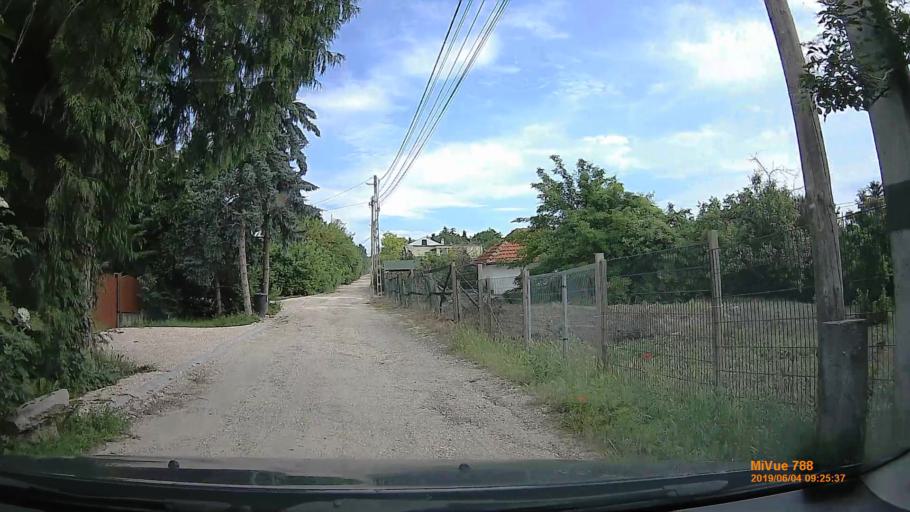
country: HU
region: Pest
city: Diosd
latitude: 47.4091
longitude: 18.9843
